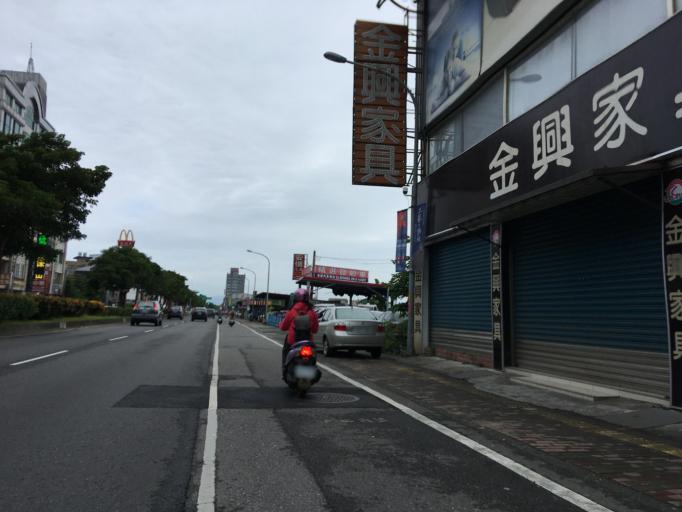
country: TW
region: Taiwan
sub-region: Yilan
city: Yilan
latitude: 24.7022
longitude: 121.7700
